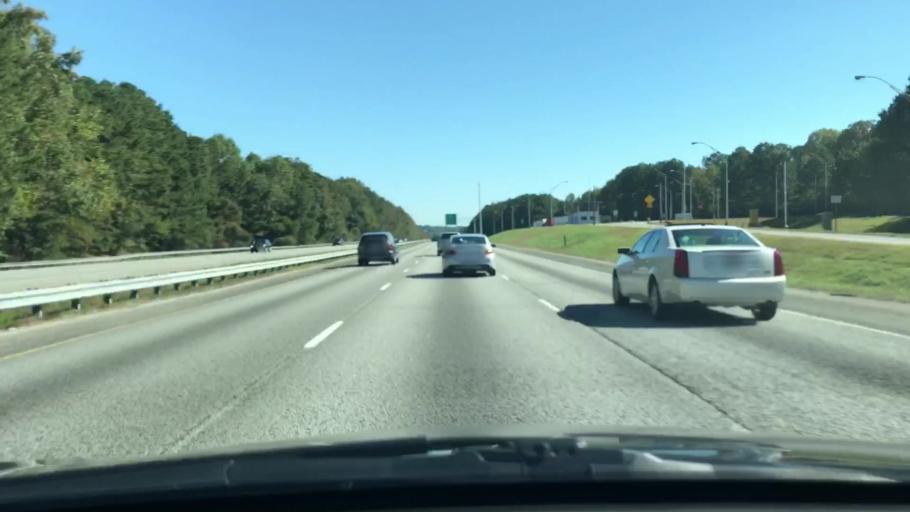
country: US
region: Georgia
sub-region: Douglas County
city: Lithia Springs
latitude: 33.7724
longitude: -84.6331
